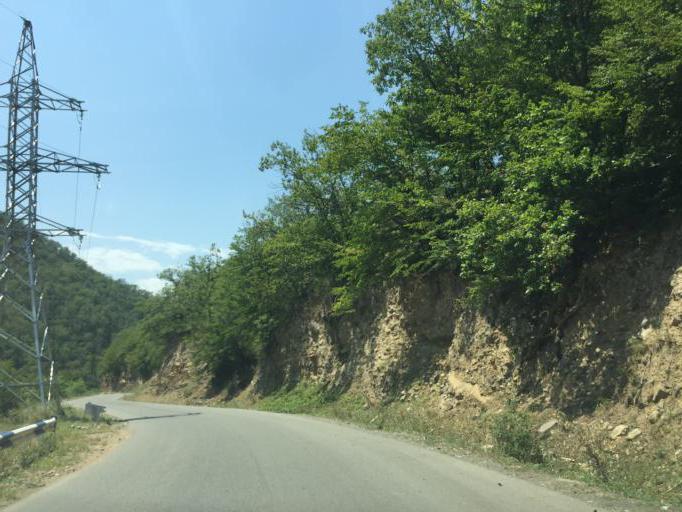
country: AZ
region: Kalbacar Rayonu
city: Kerbakhiar
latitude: 40.1351
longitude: 46.3889
